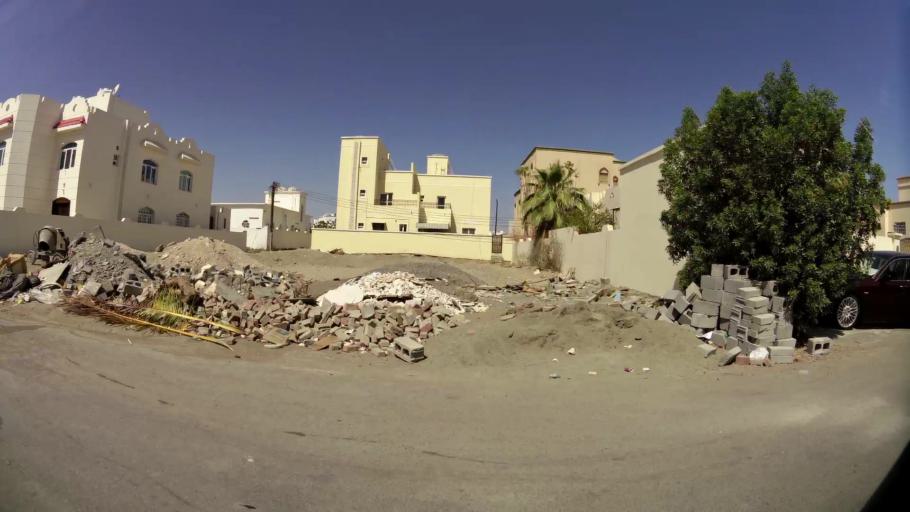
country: OM
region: Muhafazat Masqat
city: As Sib al Jadidah
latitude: 23.6031
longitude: 58.2395
